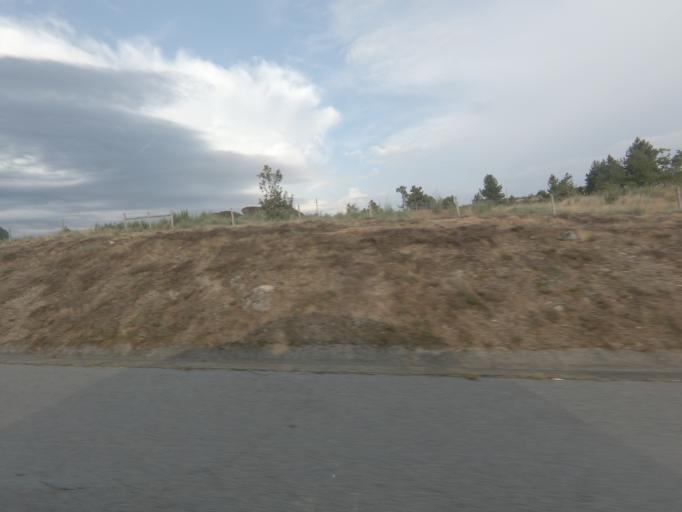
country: PT
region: Viseu
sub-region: Castro Daire
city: Castro Daire
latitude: 40.9728
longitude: -7.8879
